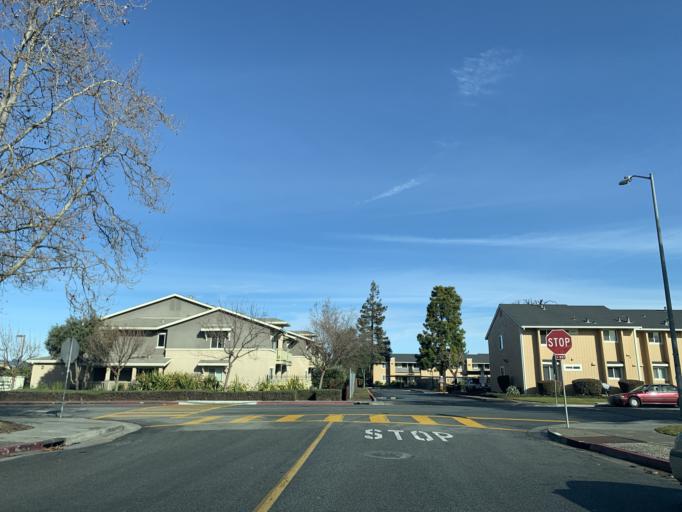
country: US
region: California
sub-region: San Benito County
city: Hollister
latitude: 36.8432
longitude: -121.3968
